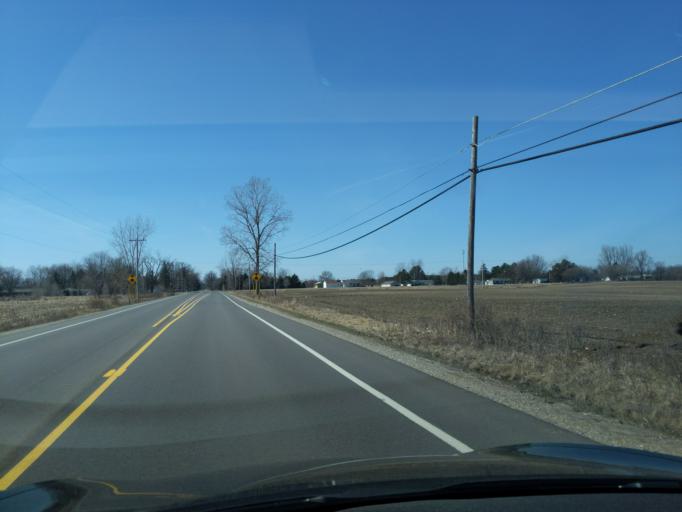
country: US
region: Michigan
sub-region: Eaton County
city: Grand Ledge
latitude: 42.7264
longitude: -84.7360
